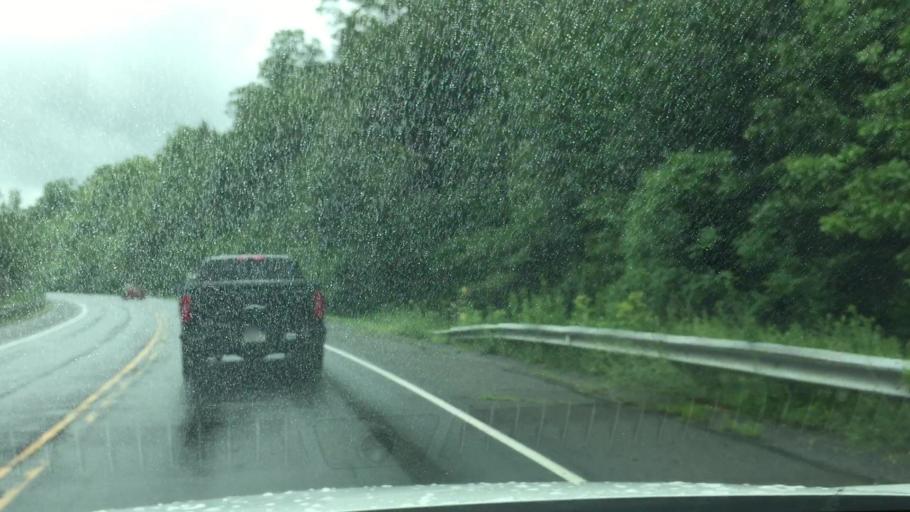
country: US
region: Massachusetts
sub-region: Berkshire County
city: Pittsfield
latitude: 42.4154
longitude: -73.2744
